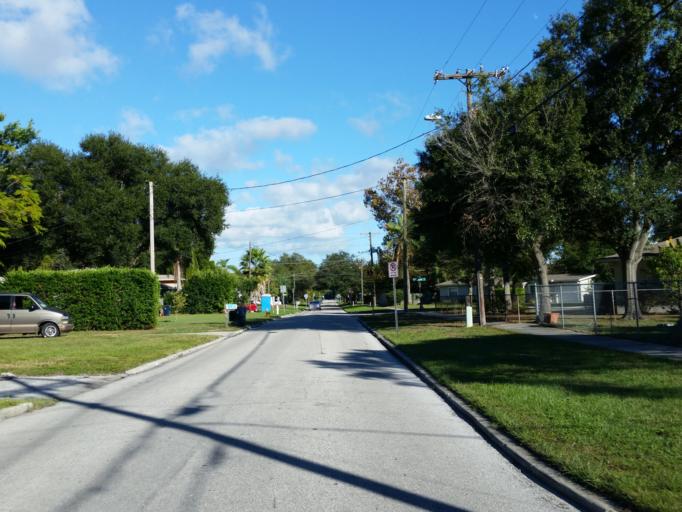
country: US
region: Florida
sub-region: Hillsborough County
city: Tampa
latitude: 27.9006
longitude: -82.5138
